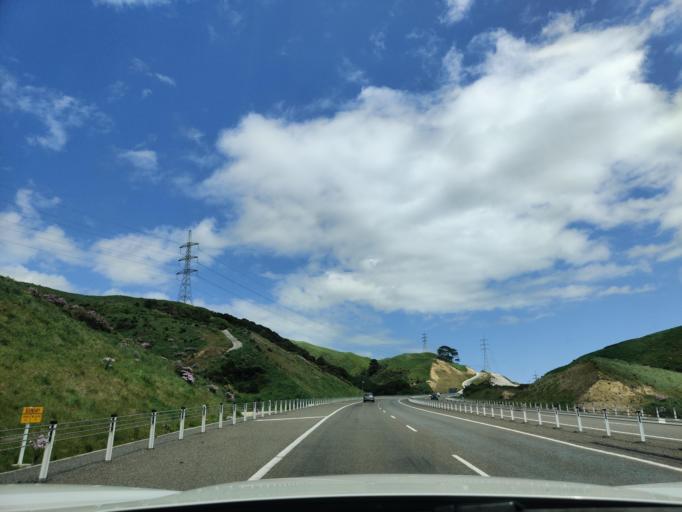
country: NZ
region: Wellington
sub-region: Porirua City
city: Porirua
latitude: -41.1487
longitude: 174.8867
